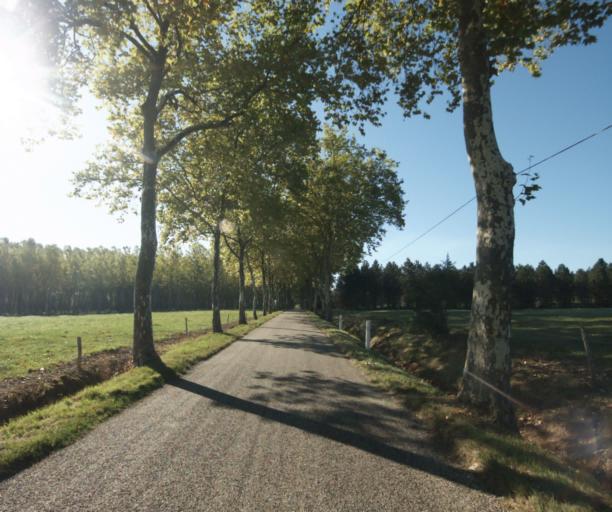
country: FR
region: Midi-Pyrenees
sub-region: Departement du Gers
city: Vic-Fezensac
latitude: 43.8327
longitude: 0.2875
